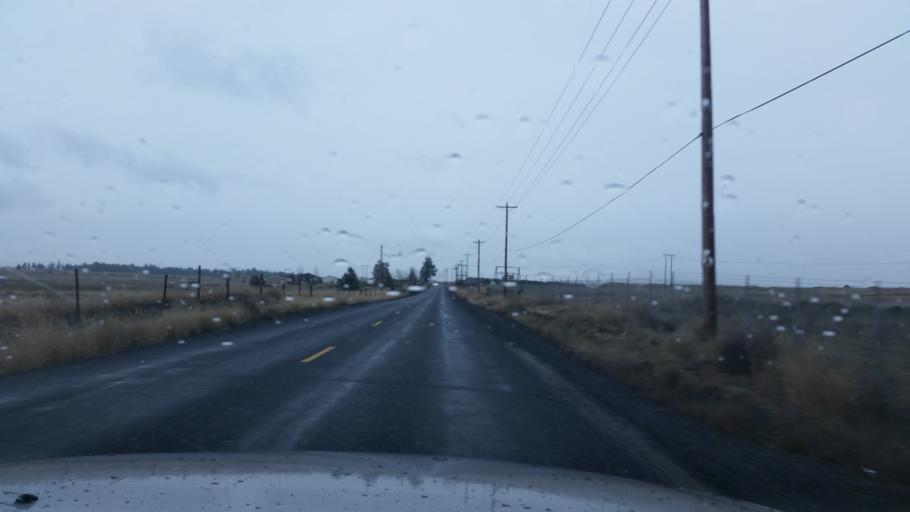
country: US
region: Washington
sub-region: Spokane County
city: Airway Heights
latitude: 47.6719
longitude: -117.5792
